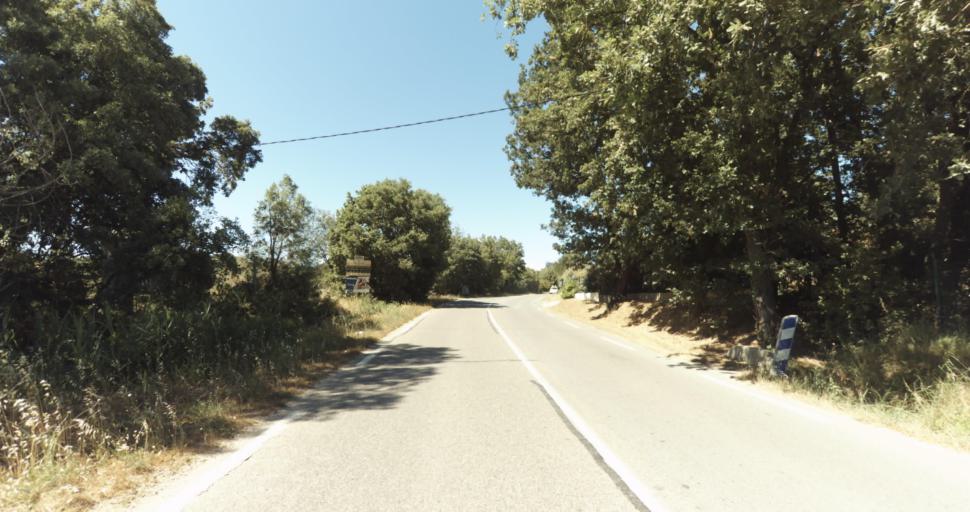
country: FR
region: Provence-Alpes-Cote d'Azur
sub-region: Departement du Var
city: Gassin
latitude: 43.2285
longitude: 6.5738
